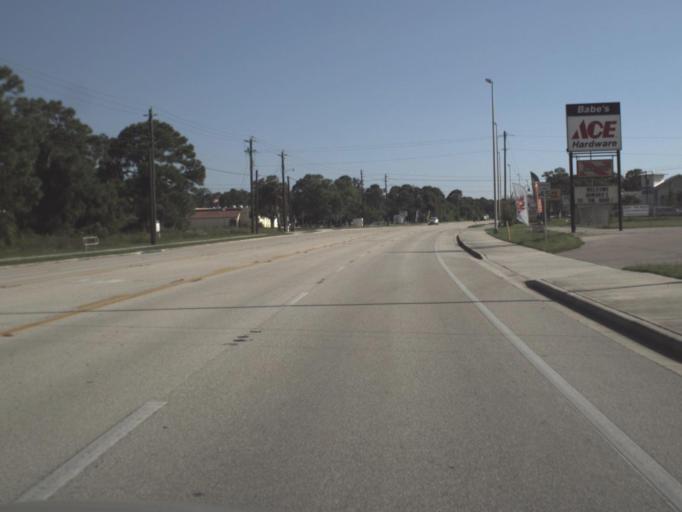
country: US
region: Florida
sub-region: Sarasota County
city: Englewood
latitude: 26.9714
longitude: -82.3532
